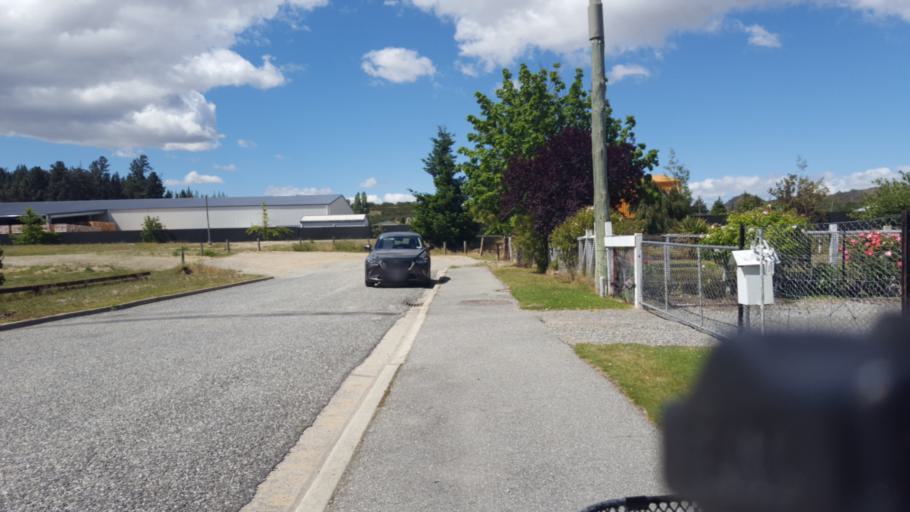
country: NZ
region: Otago
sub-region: Queenstown-Lakes District
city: Wanaka
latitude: -45.2482
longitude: 169.3967
